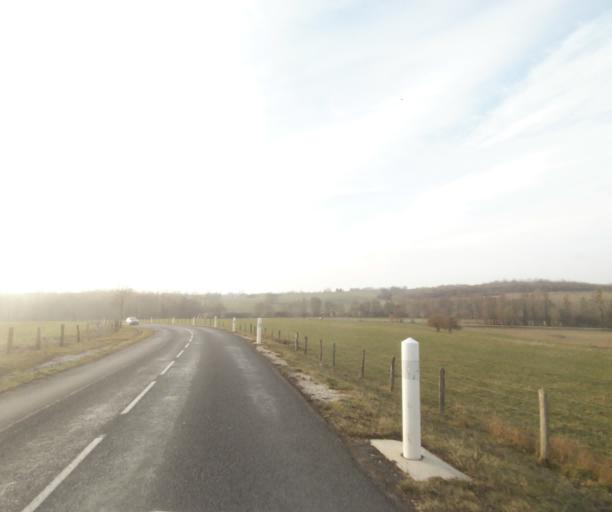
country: FR
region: Champagne-Ardenne
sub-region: Departement de la Marne
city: Sermaize-les-Bains
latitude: 48.7476
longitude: 4.9042
